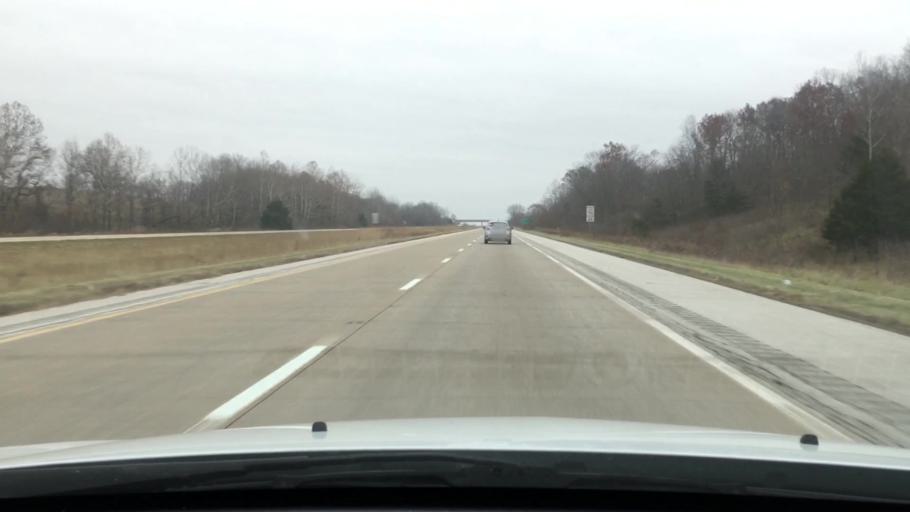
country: US
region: Illinois
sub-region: Scott County
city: Winchester
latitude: 39.6849
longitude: -90.5582
